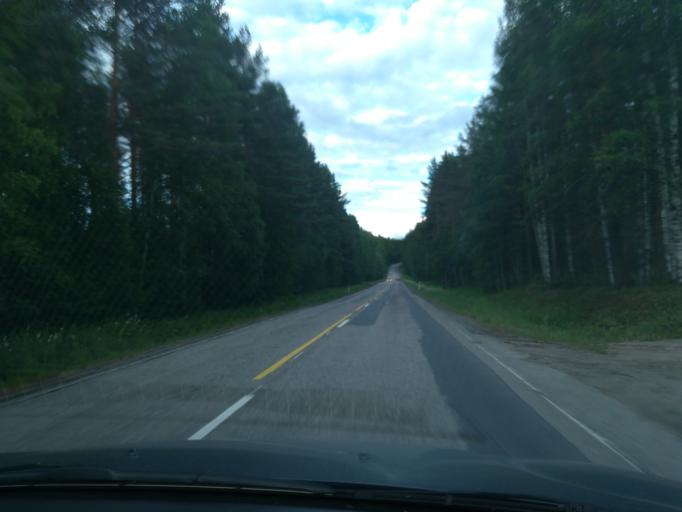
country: FI
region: Southern Savonia
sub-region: Mikkeli
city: Puumala
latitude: 61.5683
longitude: 28.0592
